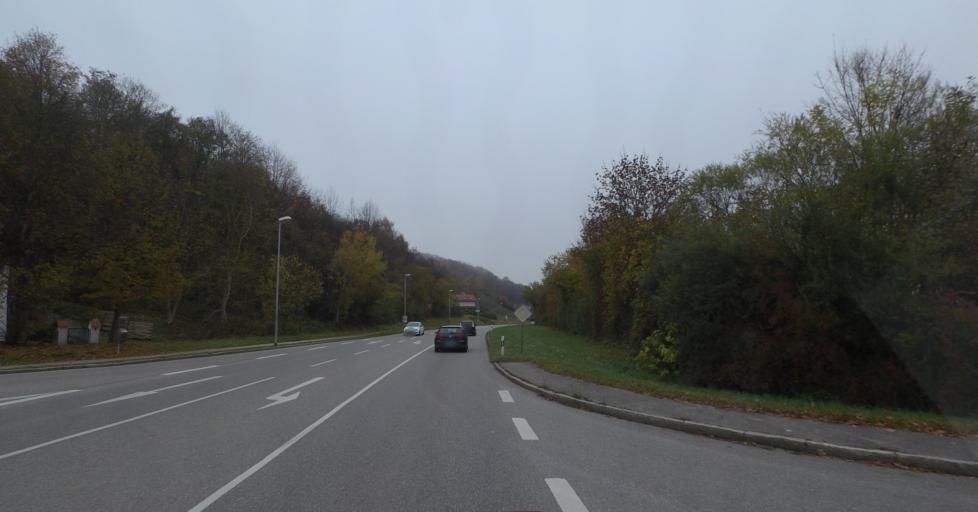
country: DE
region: Bavaria
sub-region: Upper Bavaria
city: Trostberg an der Alz
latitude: 48.0221
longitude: 12.5352
